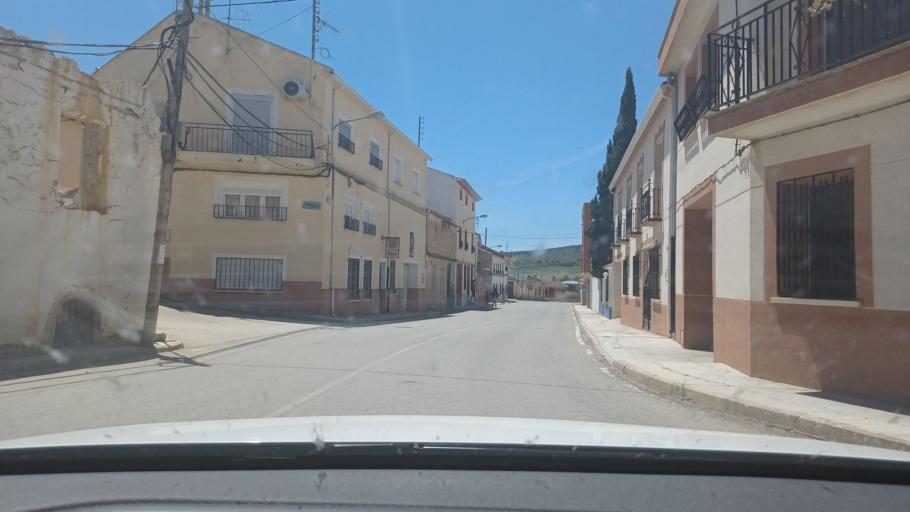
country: ES
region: Castille-La Mancha
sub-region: Provincia de Cuenca
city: Villares del Saz
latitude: 39.8394
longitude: -2.5047
